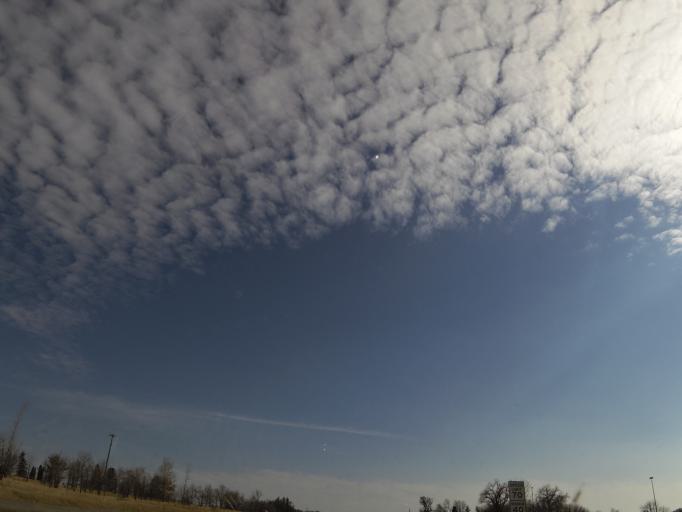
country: US
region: Minnesota
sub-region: Steele County
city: Medford
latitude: 44.1664
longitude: -93.2584
